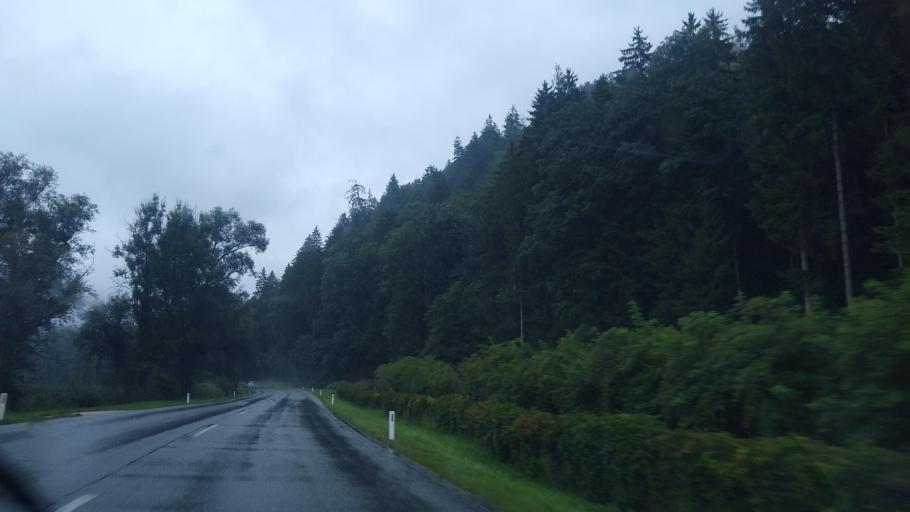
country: AT
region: Tyrol
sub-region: Politischer Bezirk Kufstein
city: Reith im Alpbachtal
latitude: 47.4170
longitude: 11.8582
